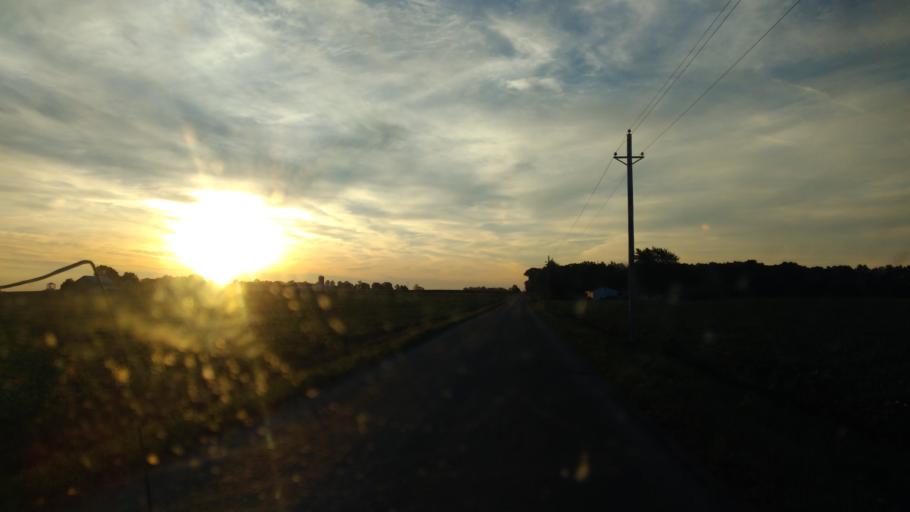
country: US
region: Indiana
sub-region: Adams County
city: Berne
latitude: 40.6706
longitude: -85.0306
